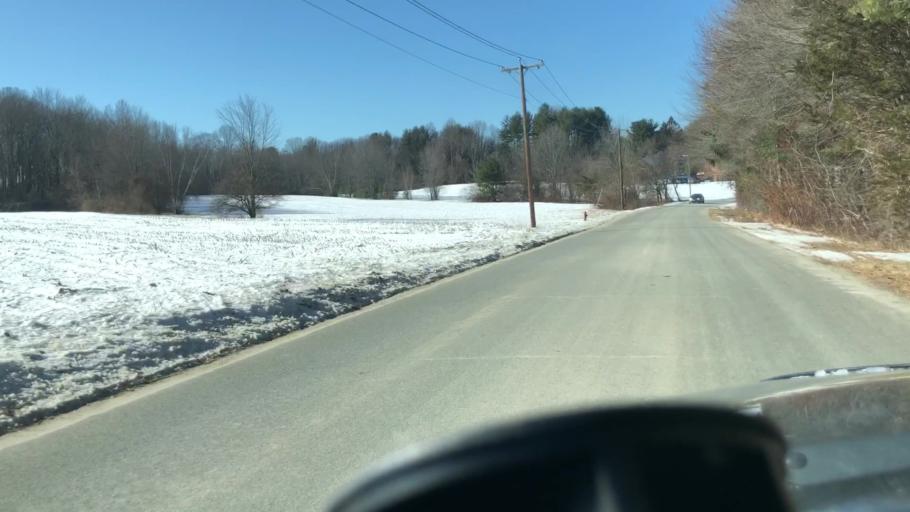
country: US
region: Massachusetts
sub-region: Hampshire County
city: Southampton
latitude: 42.2250
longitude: -72.7272
